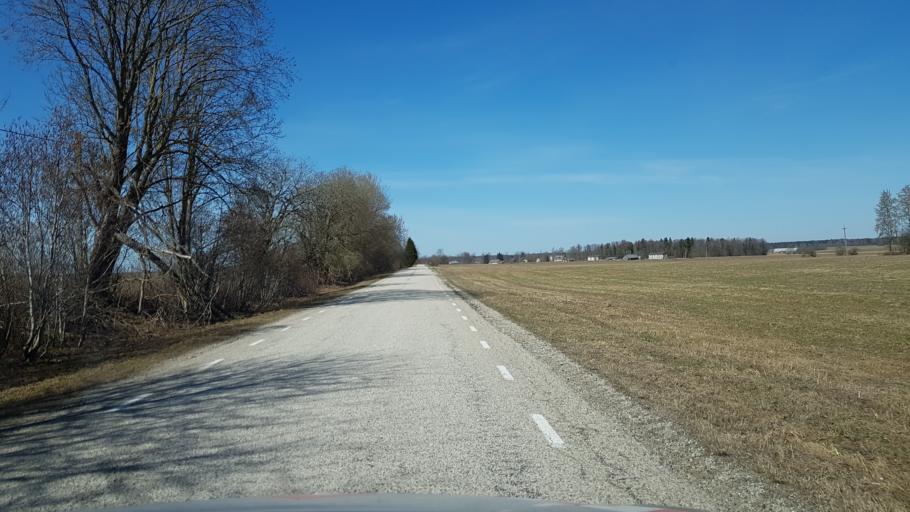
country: EE
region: Laeaene-Virumaa
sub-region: Vinni vald
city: Vinni
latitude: 59.0879
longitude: 26.5397
